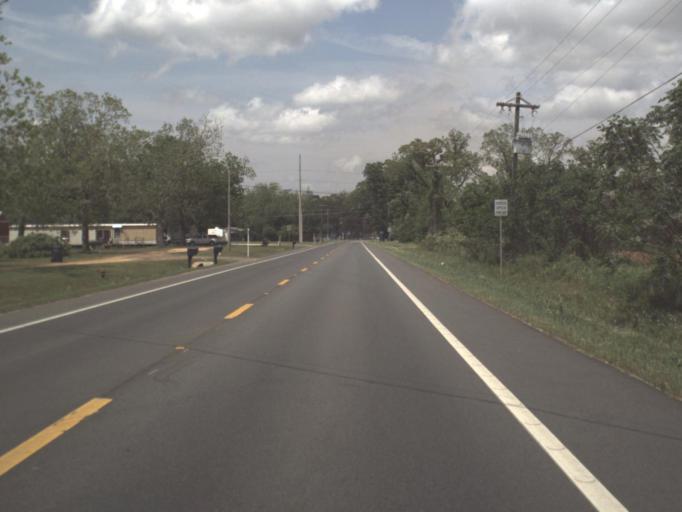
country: US
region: Florida
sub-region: Escambia County
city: Century
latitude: 30.9356
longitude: -87.1569
